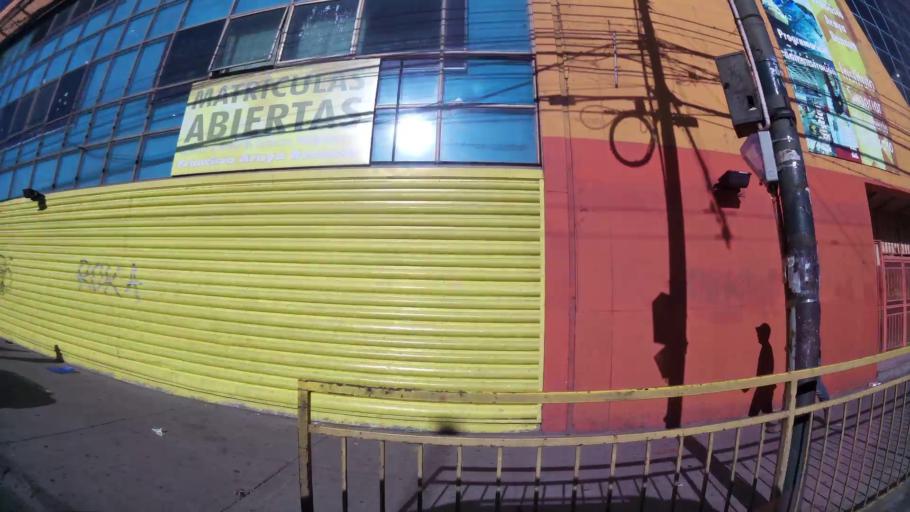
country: CL
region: Valparaiso
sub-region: Provincia de Valparaiso
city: Valparaiso
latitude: -33.0502
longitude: -71.6026
